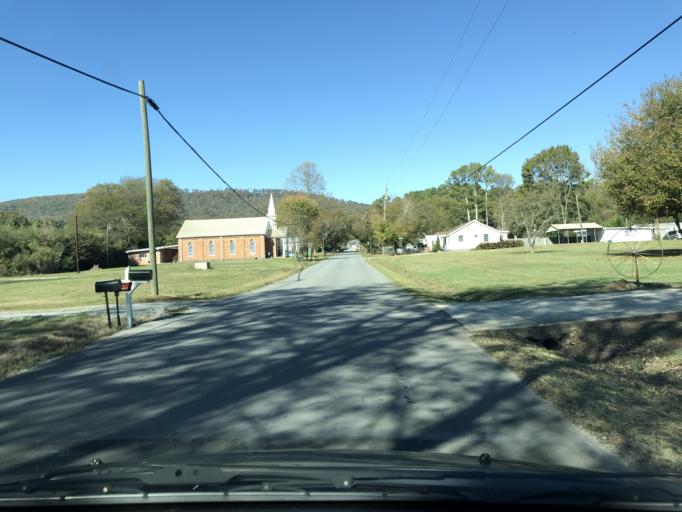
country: US
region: Georgia
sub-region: Dade County
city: Trenton
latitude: 34.9087
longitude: -85.4781
